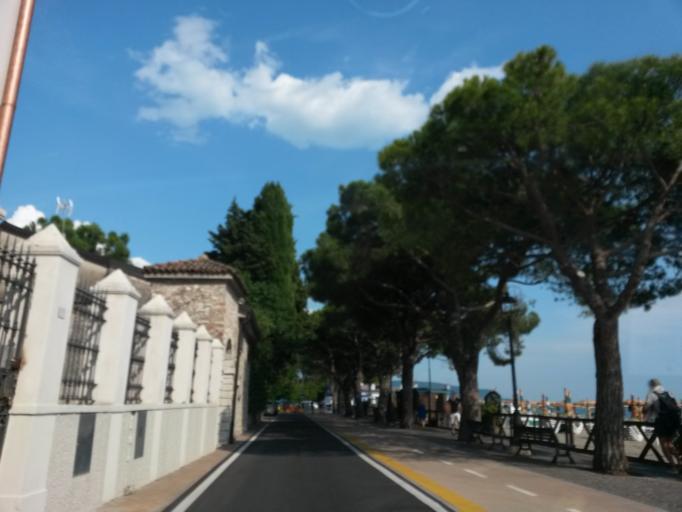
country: IT
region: Lombardy
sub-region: Provincia di Brescia
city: Toscolano Maderno
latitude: 45.6324
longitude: 10.6030
